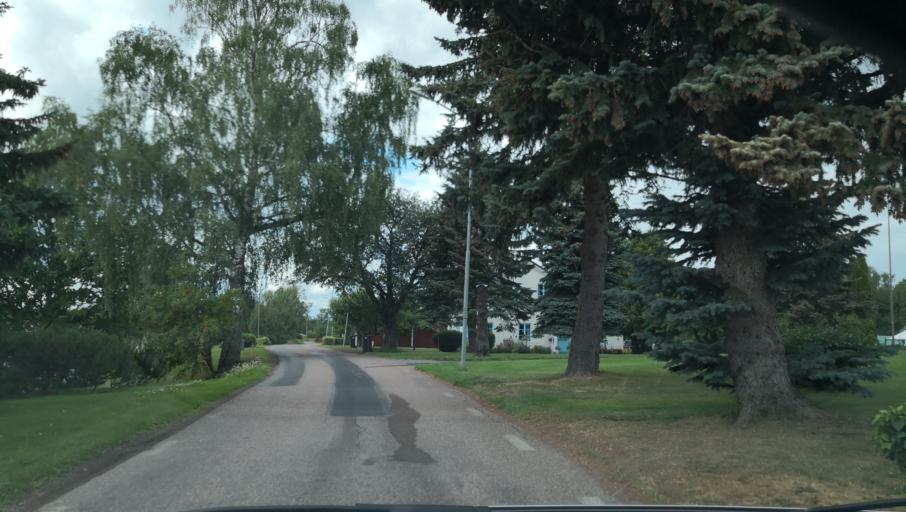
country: SE
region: Dalarna
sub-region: Borlange Kommun
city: Ornas
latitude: 60.4610
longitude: 15.5759
